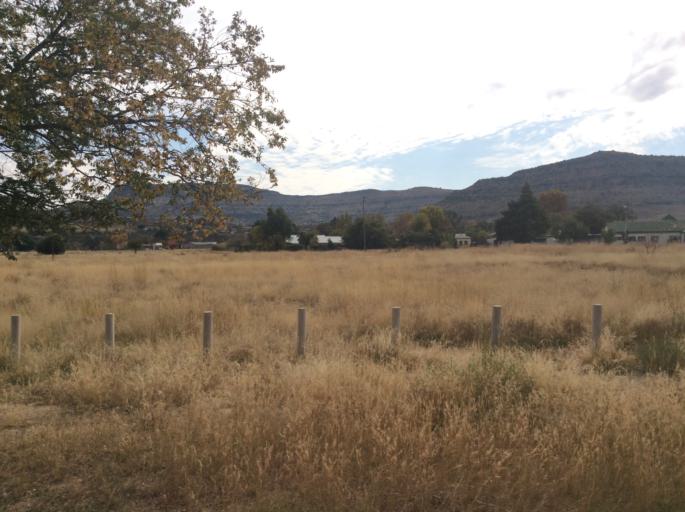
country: LS
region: Mafeteng
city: Mafeteng
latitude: -29.7314
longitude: 27.0357
